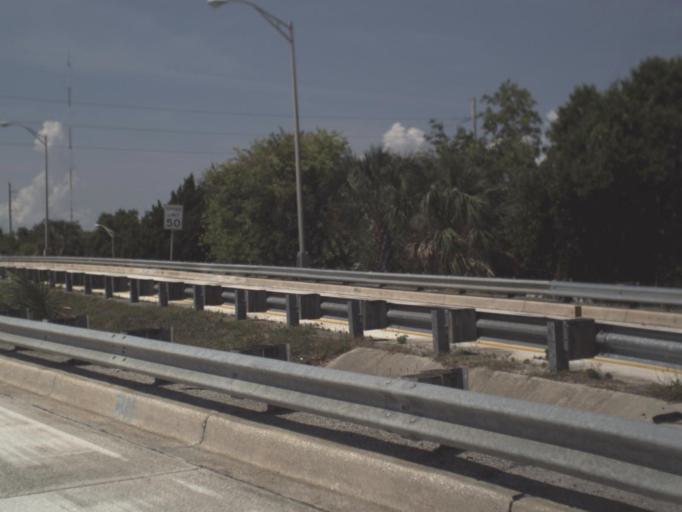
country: US
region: Florida
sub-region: Duval County
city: Jacksonville
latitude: 30.3346
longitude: -81.6368
